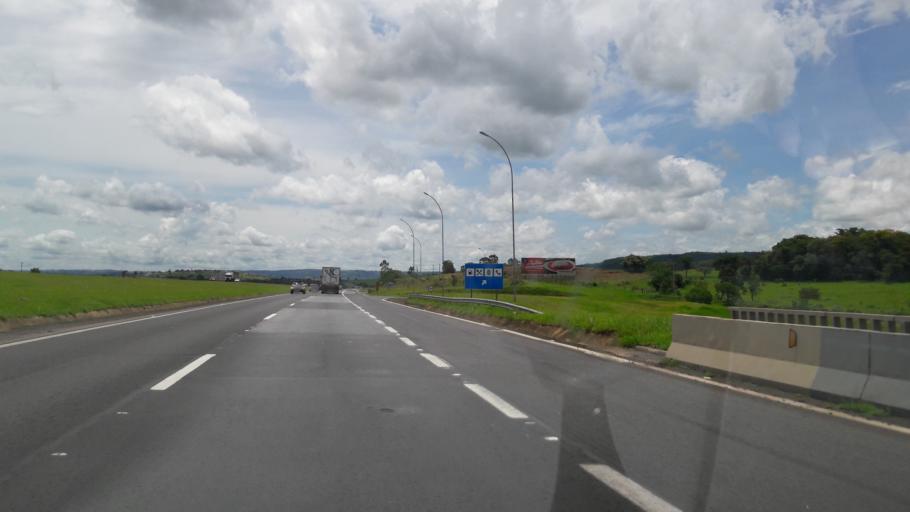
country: BR
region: Sao Paulo
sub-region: Itatinga
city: Itatinga
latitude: -23.1568
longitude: -48.3740
